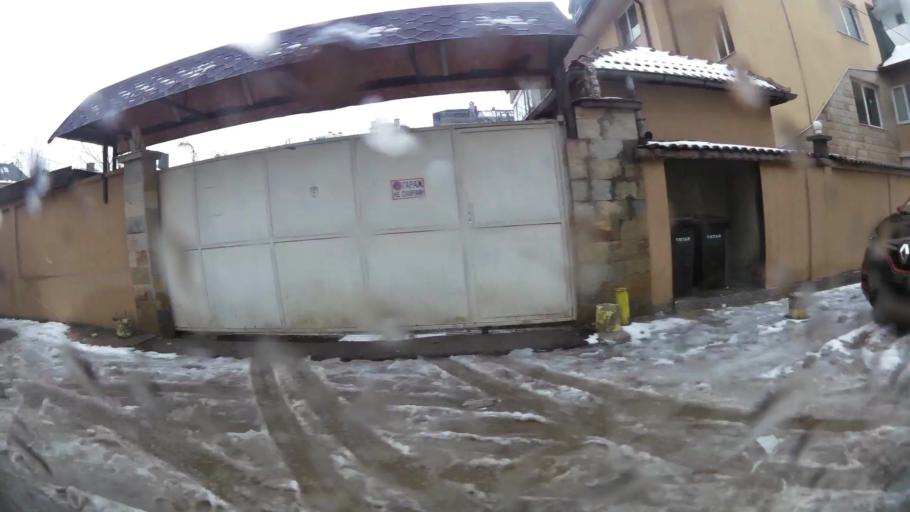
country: BG
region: Sofia-Capital
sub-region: Stolichna Obshtina
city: Sofia
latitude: 42.6614
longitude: 23.2811
